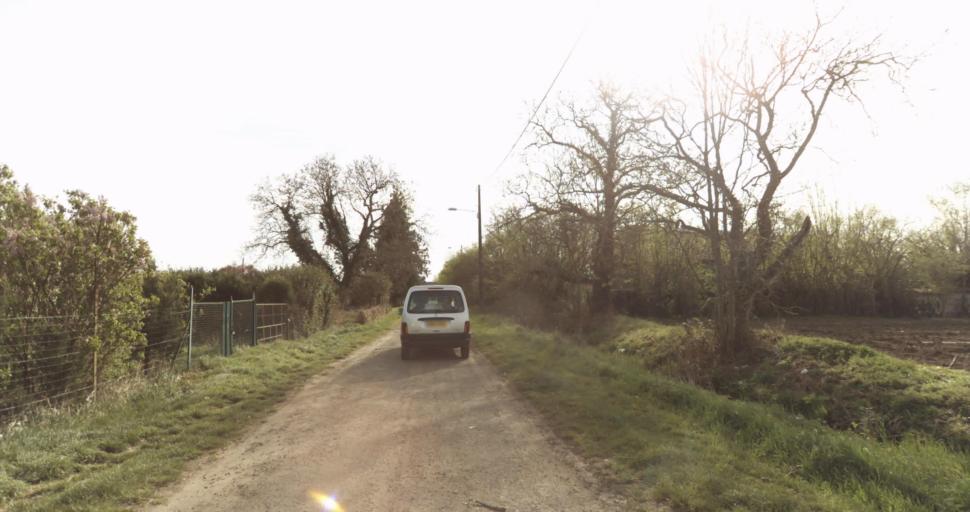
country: FR
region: Auvergne
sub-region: Departement du Puy-de-Dome
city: Cebazat
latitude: 45.8315
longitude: 3.1123
